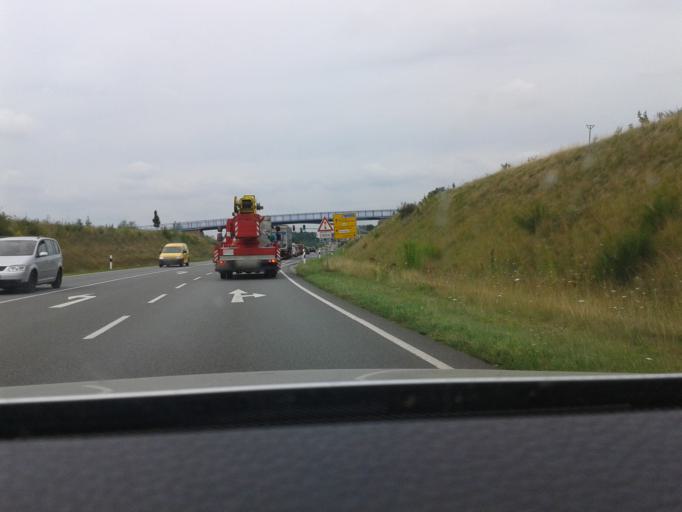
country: DE
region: Lower Saxony
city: Burgdorf
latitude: 52.4548
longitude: 10.0241
